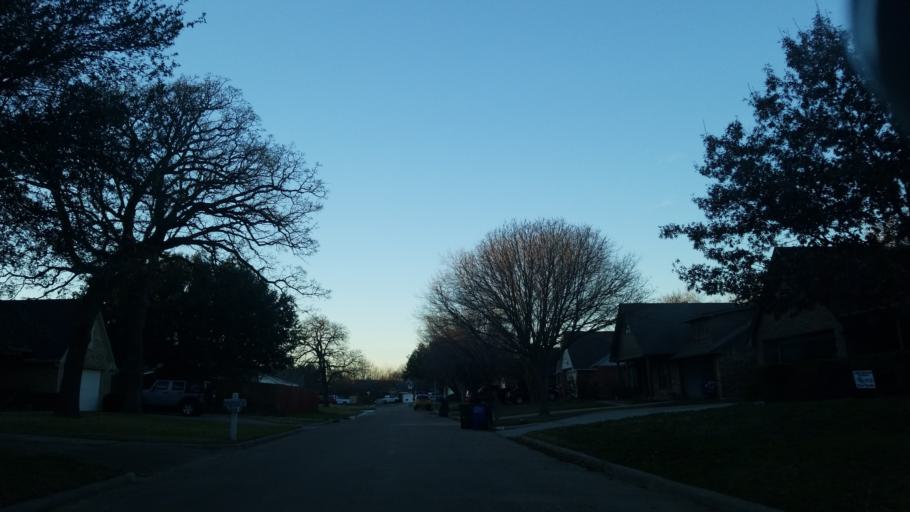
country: US
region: Texas
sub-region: Denton County
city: Hickory Creek
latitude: 33.1378
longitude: -97.0536
